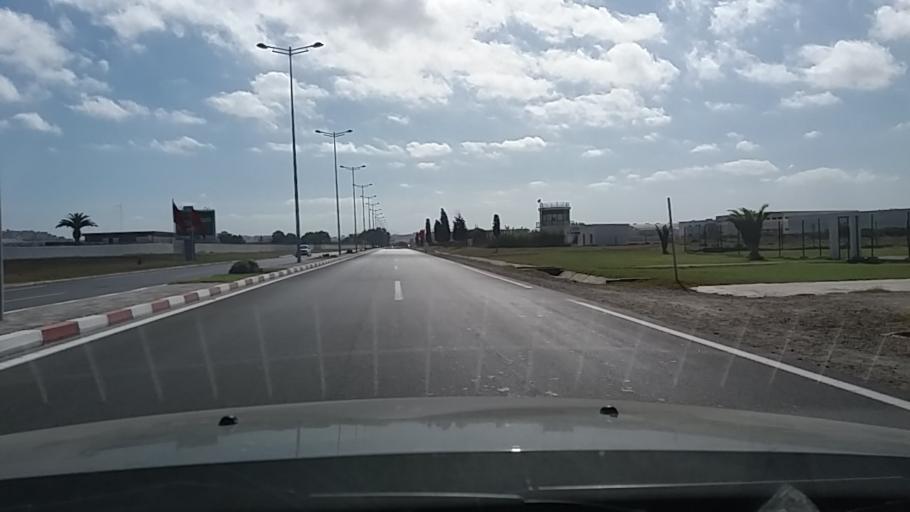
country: MA
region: Tanger-Tetouan
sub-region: Tanger-Assilah
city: Boukhalef
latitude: 35.7271
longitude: -5.9073
